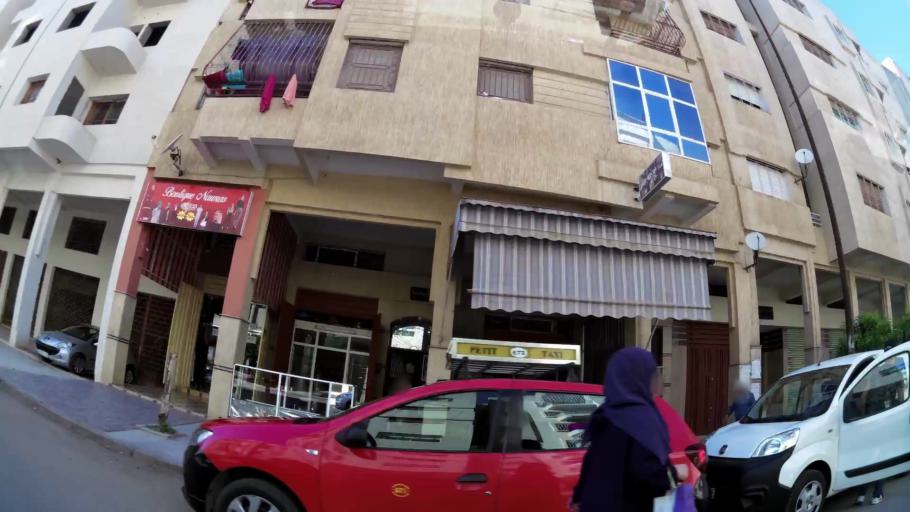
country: MA
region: Fes-Boulemane
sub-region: Fes
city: Fes
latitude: 34.0149
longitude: -4.9769
